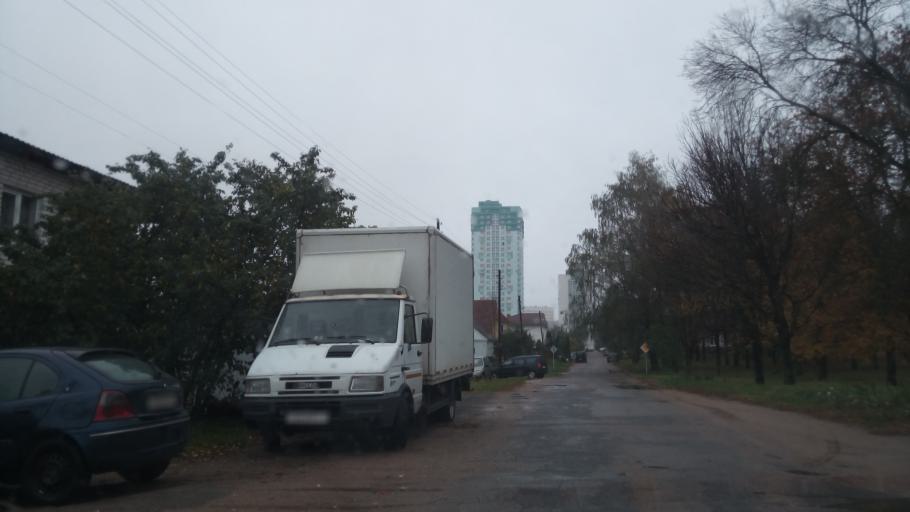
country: BY
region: Minsk
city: Minsk
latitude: 53.9419
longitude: 27.5898
